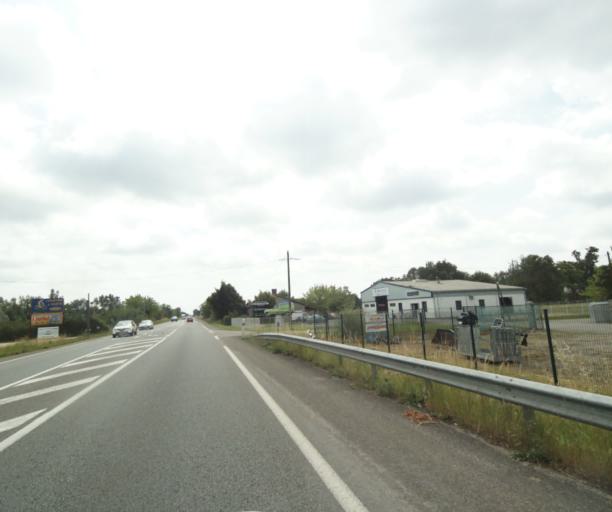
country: FR
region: Midi-Pyrenees
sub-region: Departement du Tarn-et-Garonne
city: Albias
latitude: 44.0567
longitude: 1.4046
